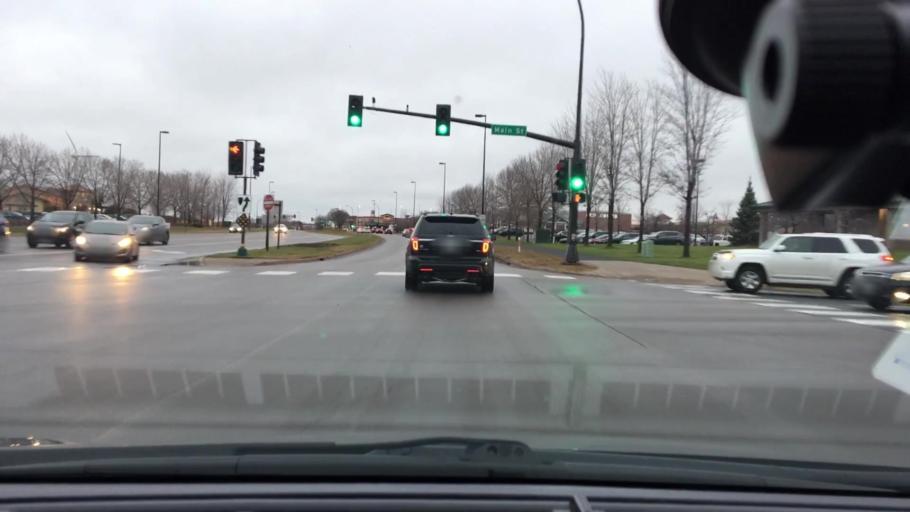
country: US
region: Minnesota
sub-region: Hennepin County
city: Maple Grove
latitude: 45.0945
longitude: -93.4417
